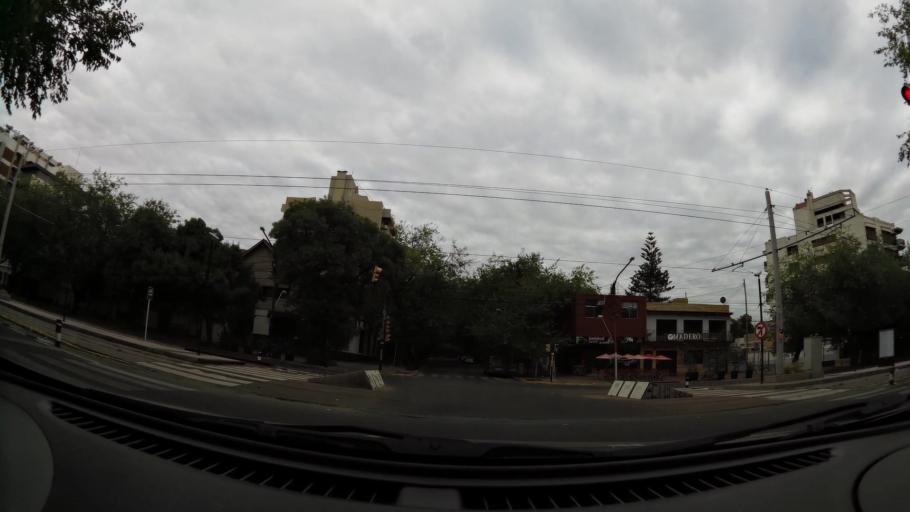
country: AR
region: Mendoza
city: Mendoza
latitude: -32.8906
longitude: -68.8535
